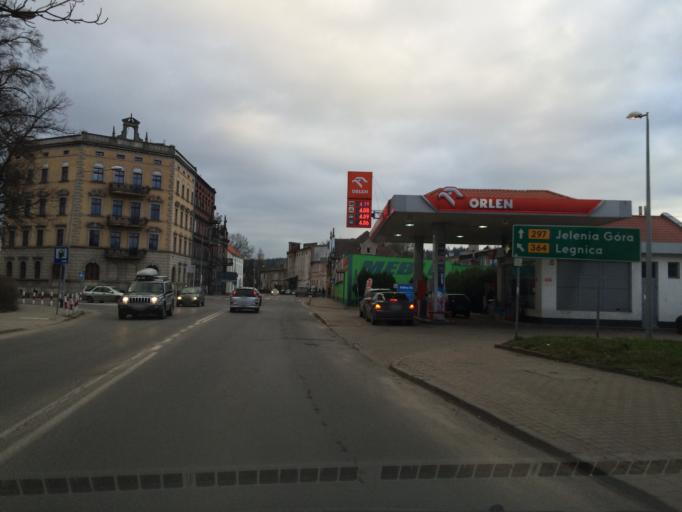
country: PL
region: Lower Silesian Voivodeship
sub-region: Powiat lwowecki
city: Lwowek Slaski
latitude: 51.1090
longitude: 15.5915
